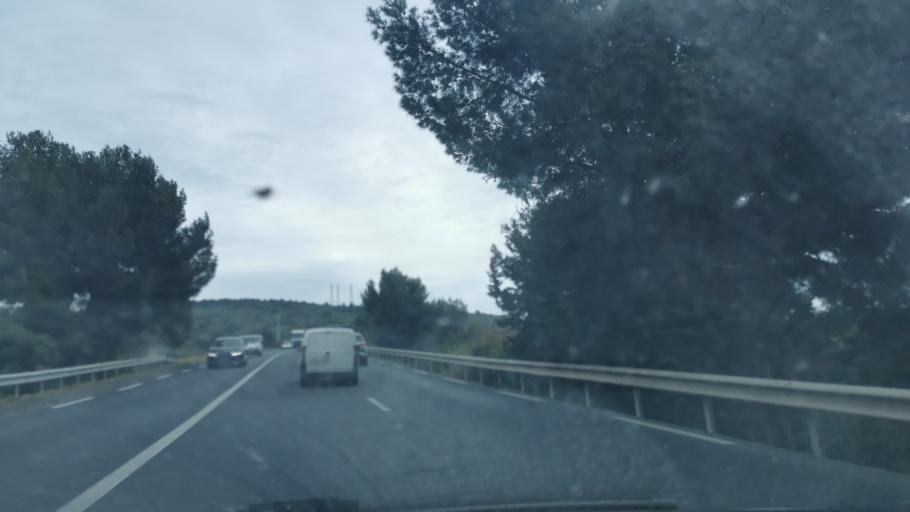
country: FR
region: Languedoc-Roussillon
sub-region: Departement de l'Herault
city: Balaruc-le-Vieux
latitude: 43.4568
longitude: 3.7008
